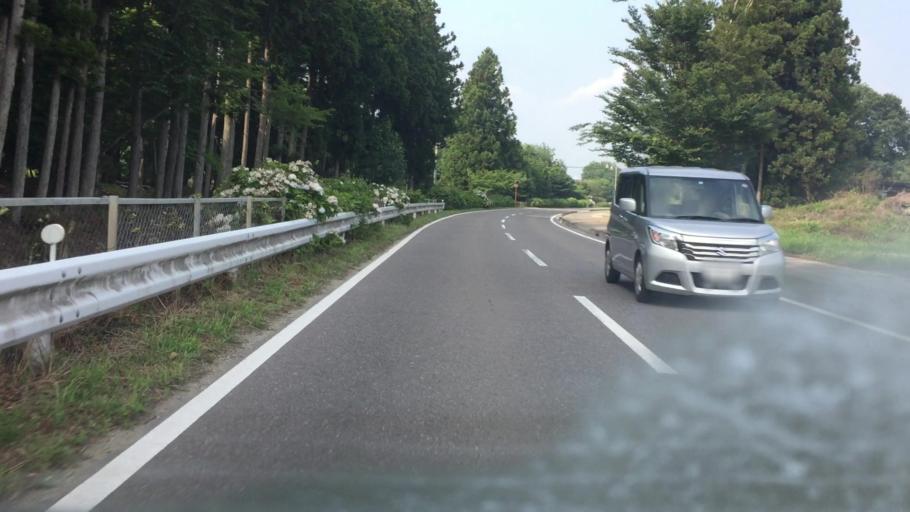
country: JP
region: Tochigi
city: Kuroiso
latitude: 36.9876
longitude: 139.9880
